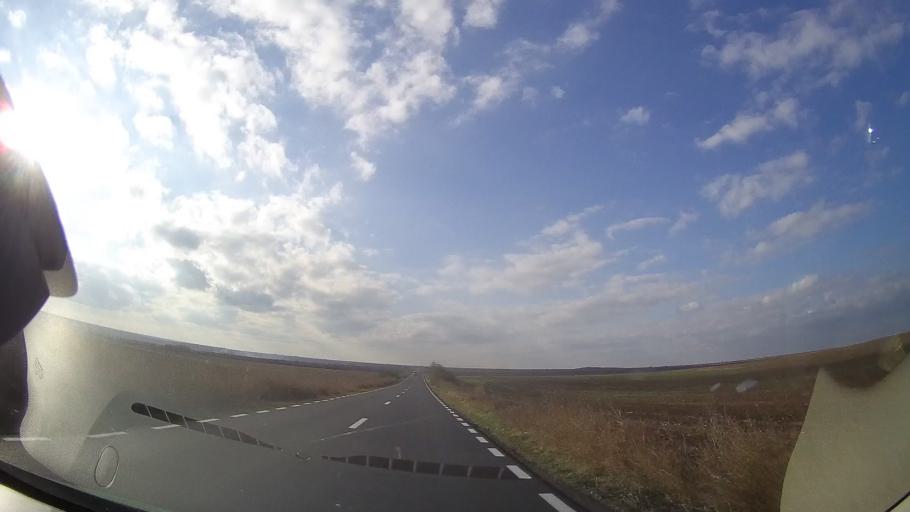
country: RO
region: Constanta
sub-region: Comuna Limanu
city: Limanu
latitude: 43.8241
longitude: 28.5115
